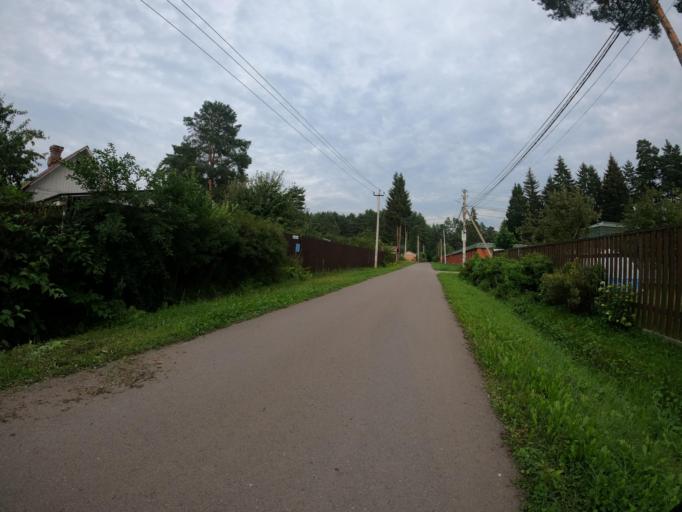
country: RU
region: Moskovskaya
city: Bykovo
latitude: 55.6472
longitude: 38.1077
